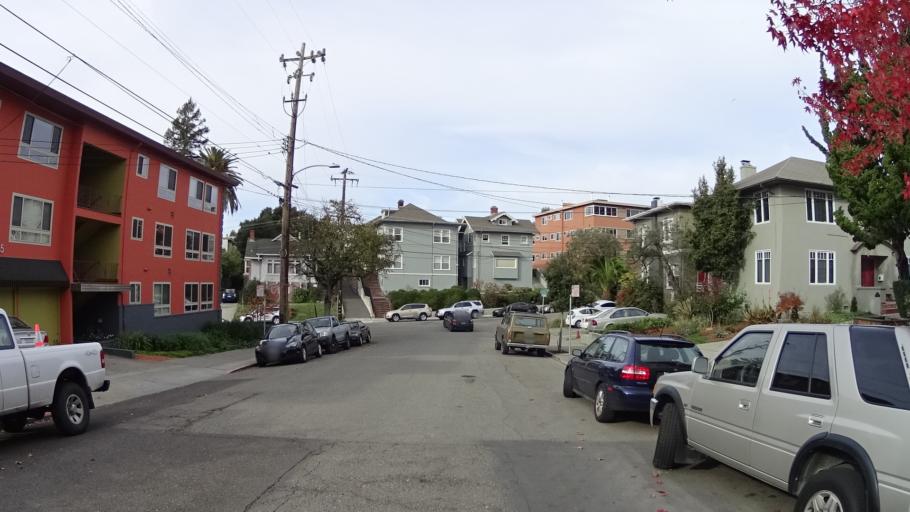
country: US
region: California
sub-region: Alameda County
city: Oakland
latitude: 37.8117
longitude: -122.2541
